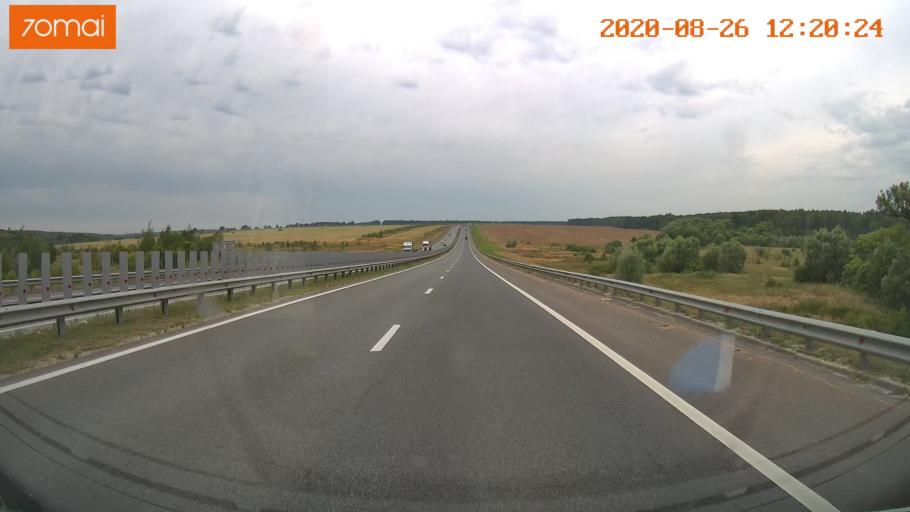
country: RU
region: Rjazan
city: Murmino
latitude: 54.4858
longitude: 39.9695
